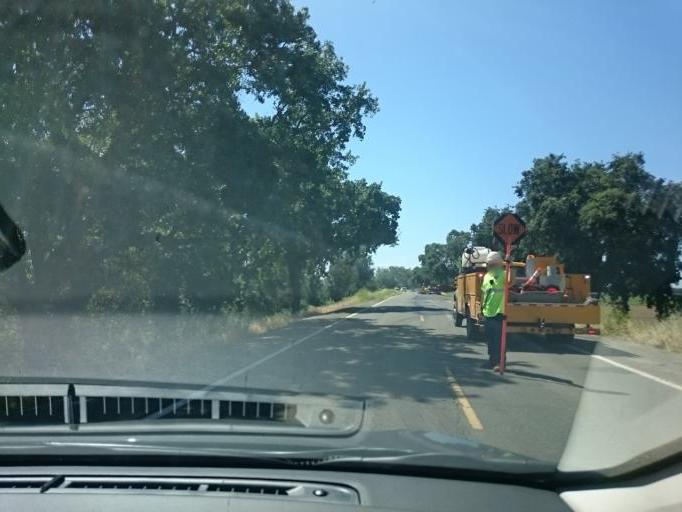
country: US
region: California
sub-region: Yolo County
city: West Sacramento
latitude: 38.4927
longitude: -121.5572
